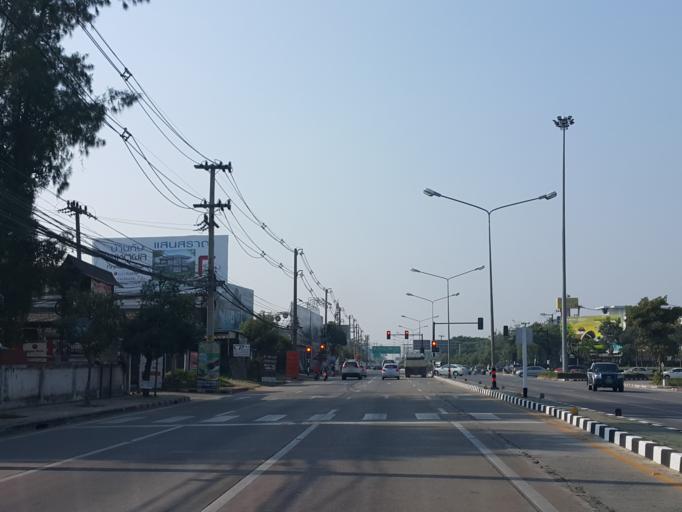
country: TH
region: Chiang Mai
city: Hang Dong
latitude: 18.7276
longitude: 98.9489
